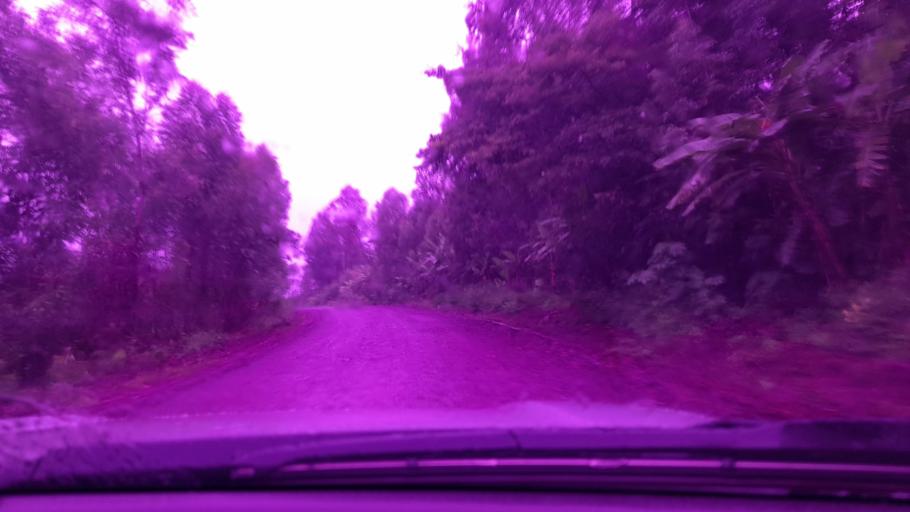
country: ET
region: Oromiya
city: Metu
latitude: 8.3350
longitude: 35.6061
